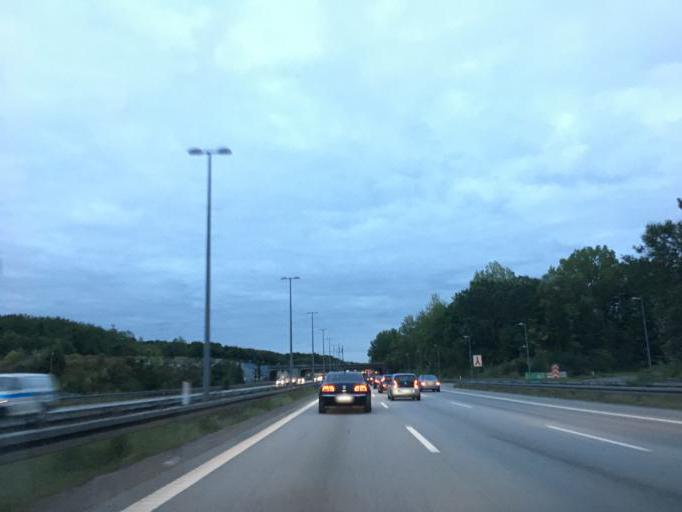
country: DK
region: Capital Region
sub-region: Glostrup Kommune
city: Glostrup
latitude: 55.6677
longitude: 12.4223
